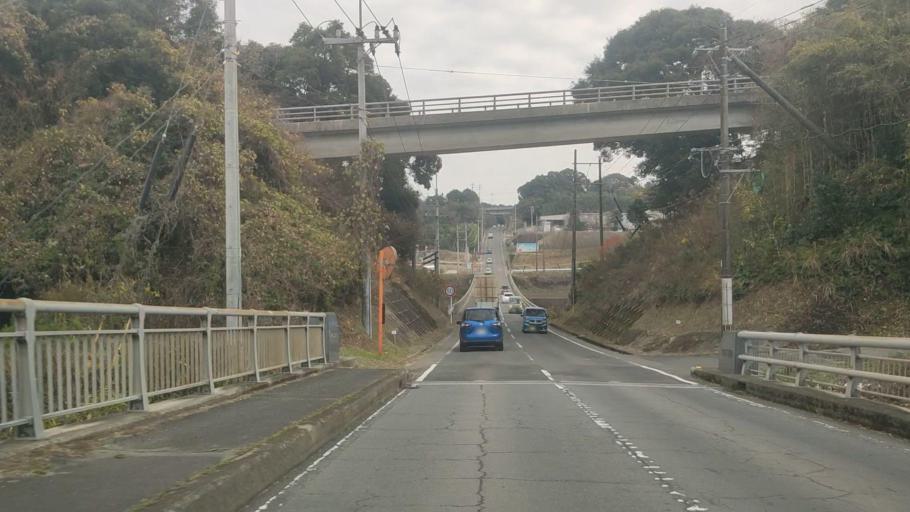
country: JP
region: Nagasaki
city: Shimabara
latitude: 32.8476
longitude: 130.2195
